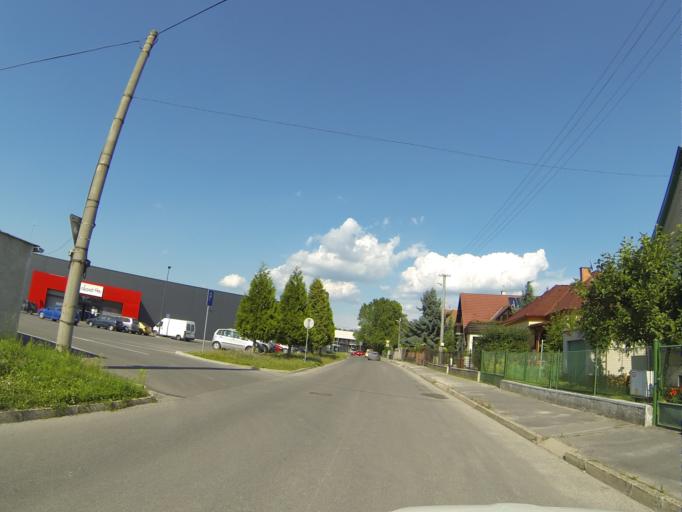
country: SK
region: Nitriansky
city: Bojnice
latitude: 48.7762
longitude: 18.6005
